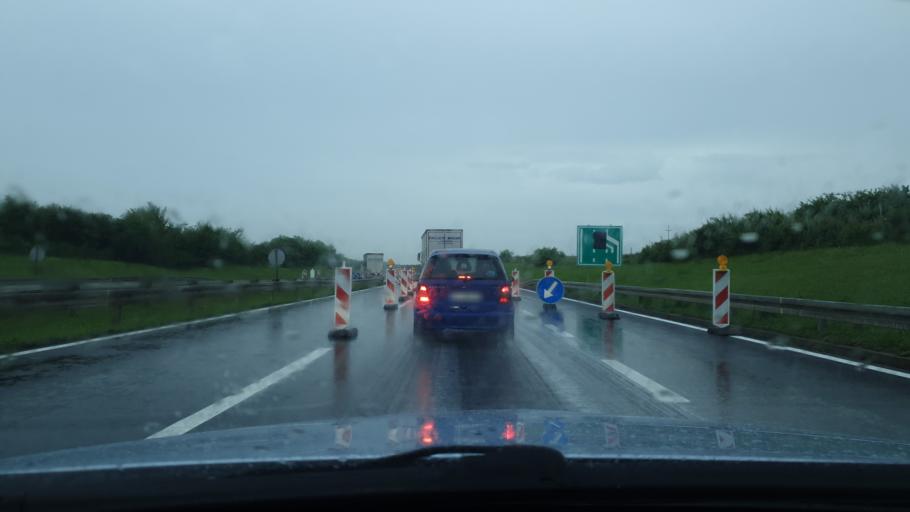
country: RS
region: Central Serbia
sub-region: Nisavski Okrug
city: Razanj
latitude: 43.7085
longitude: 21.5346
